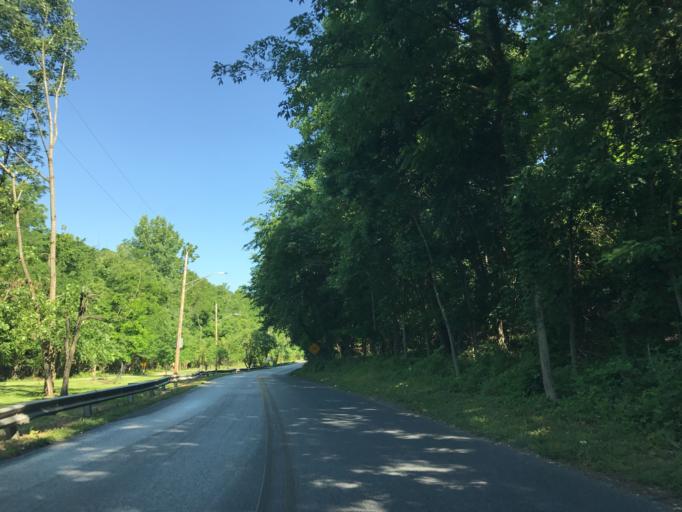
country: US
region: Maryland
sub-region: Baltimore County
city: Charlestown
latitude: 39.3007
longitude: -76.6720
